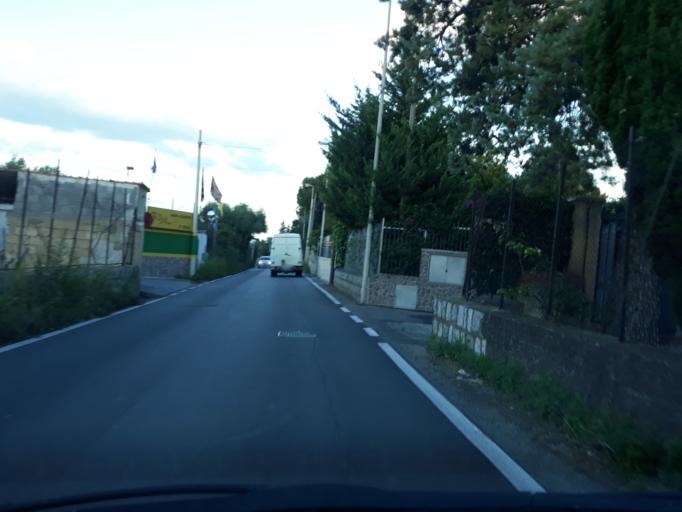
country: IT
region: Sicily
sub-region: Palermo
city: Villa Ciambra
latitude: 38.0831
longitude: 13.3243
